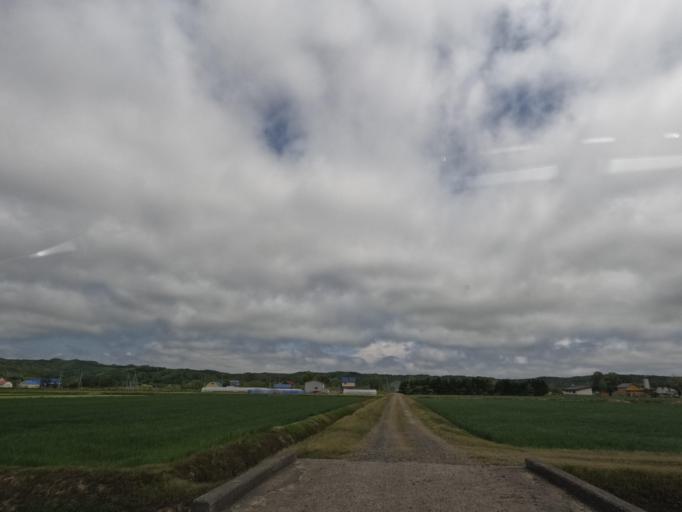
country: JP
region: Hokkaido
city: Tobetsu
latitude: 43.2666
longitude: 141.5248
